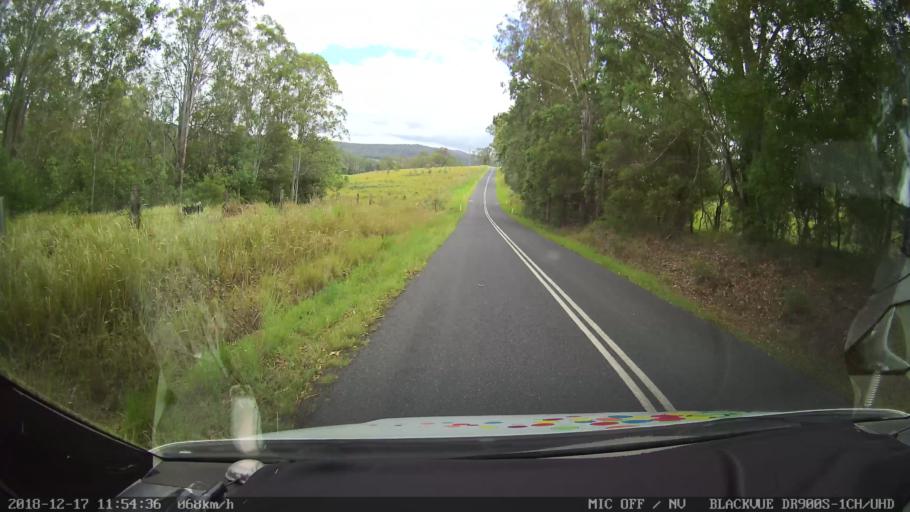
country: AU
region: New South Wales
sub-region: Kyogle
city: Kyogle
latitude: -28.5645
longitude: 152.5826
